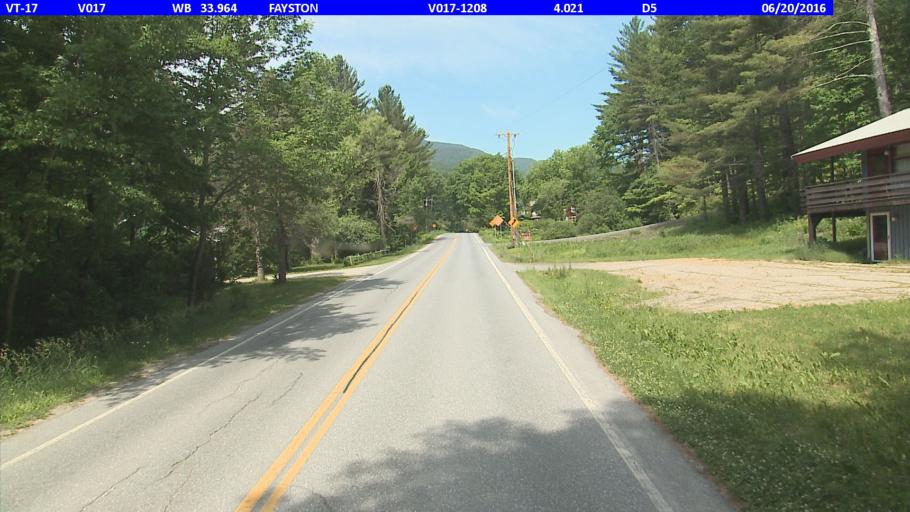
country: US
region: Vermont
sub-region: Washington County
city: Waterbury
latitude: 44.1864
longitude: -72.8762
